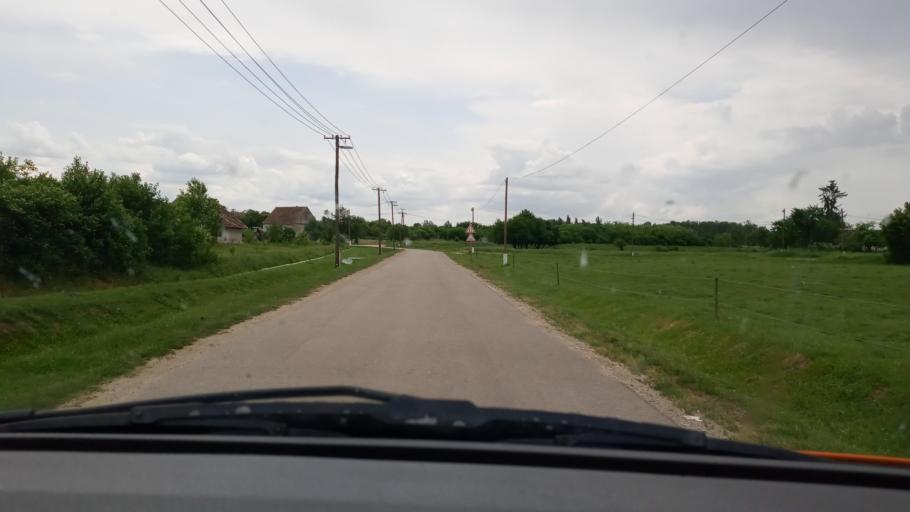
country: HU
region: Baranya
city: Vajszlo
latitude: 45.8228
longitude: 17.9935
